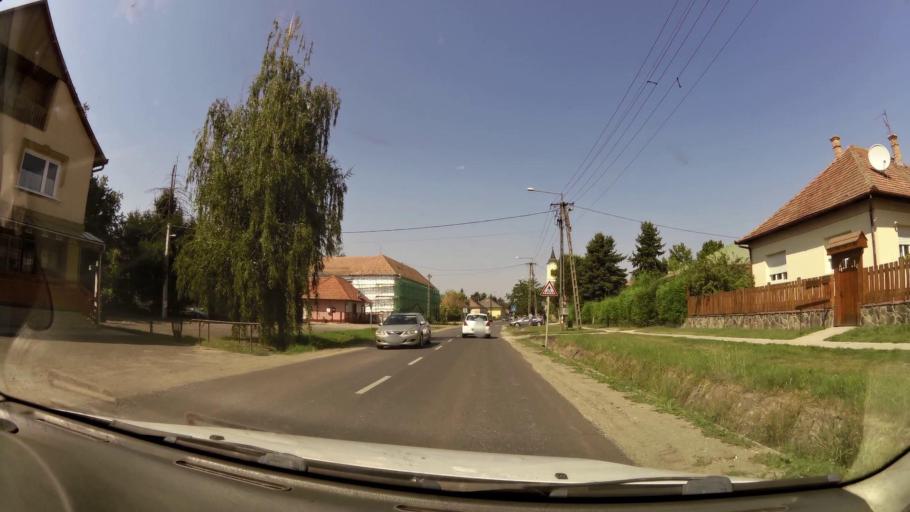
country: HU
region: Pest
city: Tapiobicske
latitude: 47.3606
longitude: 19.6895
